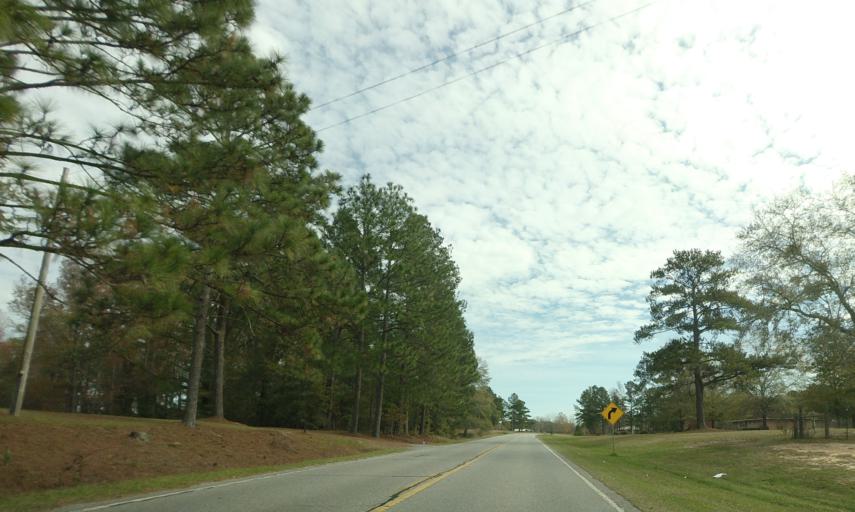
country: US
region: Georgia
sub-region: Bleckley County
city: Cochran
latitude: 32.3993
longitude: -83.2918
